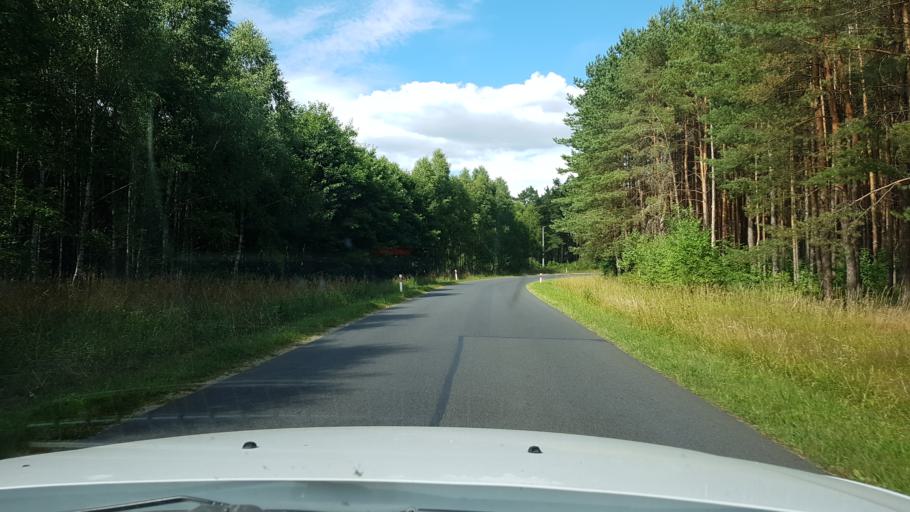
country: PL
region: West Pomeranian Voivodeship
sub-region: Powiat walecki
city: Miroslawiec
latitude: 53.4041
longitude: 15.9836
